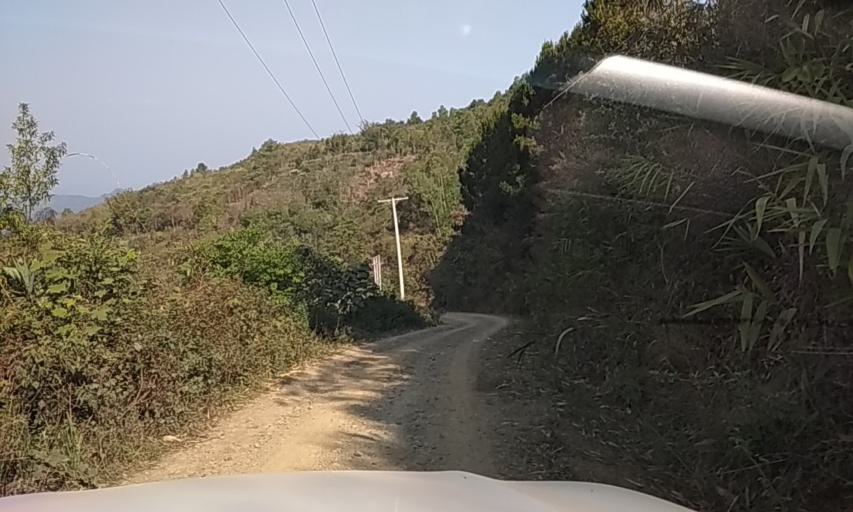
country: LA
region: Phongsali
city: Phongsali
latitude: 21.6921
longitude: 102.0977
